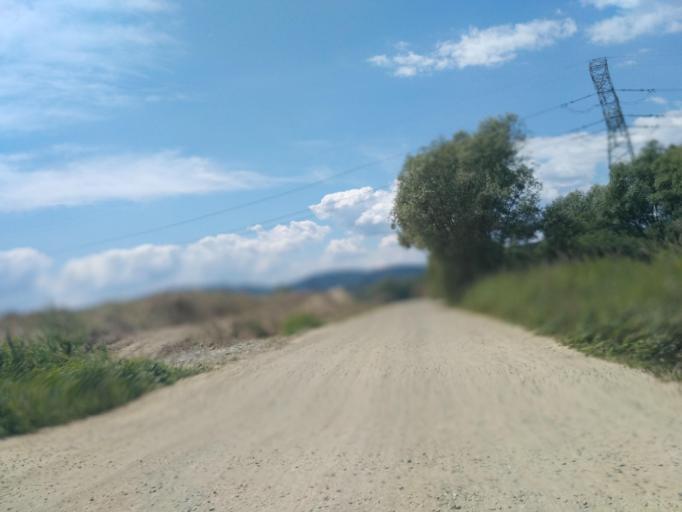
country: PL
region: Subcarpathian Voivodeship
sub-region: Powiat debicki
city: Brzostek
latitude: 49.8556
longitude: 21.4046
